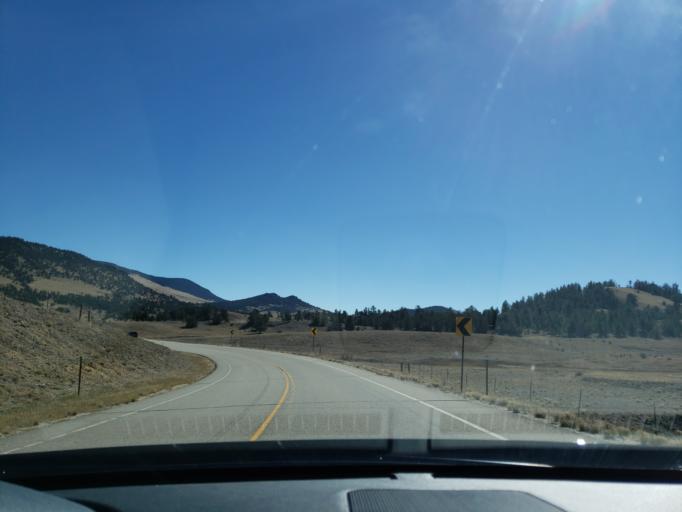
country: US
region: Colorado
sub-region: Chaffee County
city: Buena Vista
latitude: 38.8637
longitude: -105.6635
